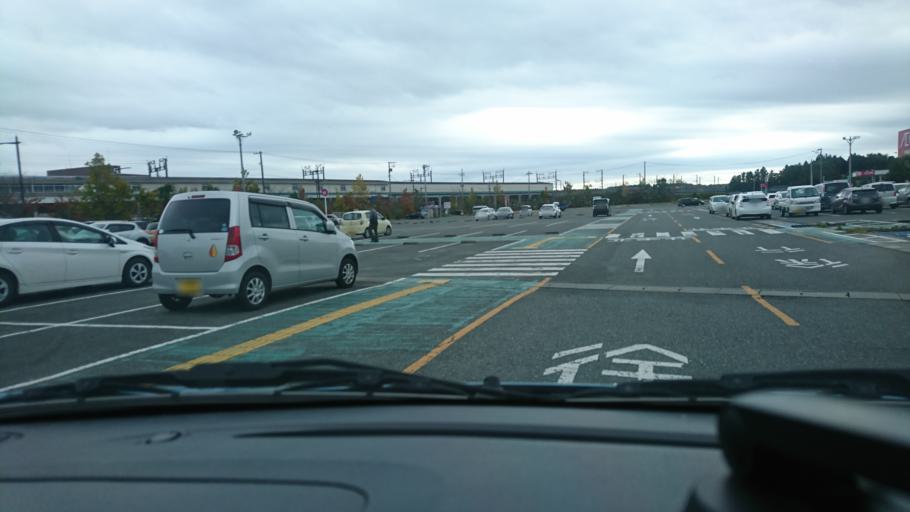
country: JP
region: Iwate
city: Ichinoseki
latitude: 38.7495
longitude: 141.0701
